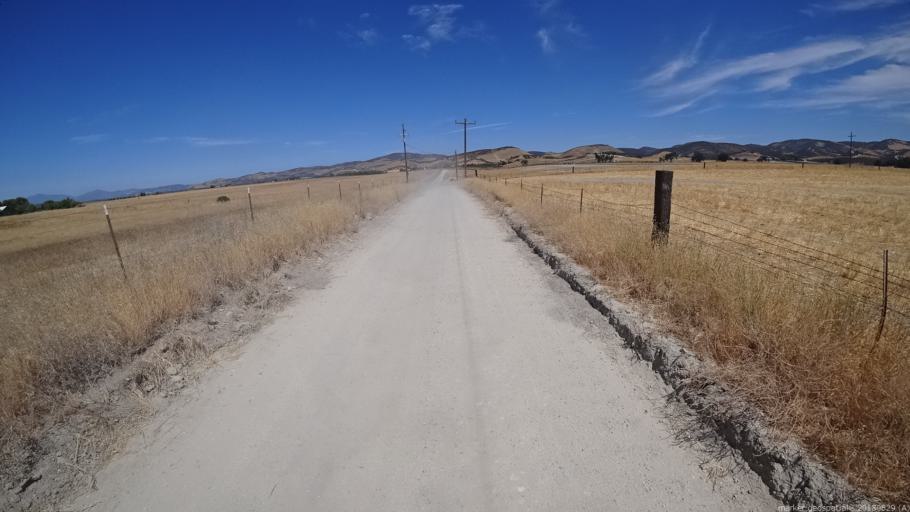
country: US
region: California
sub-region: Monterey County
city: King City
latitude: 35.9432
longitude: -121.0731
